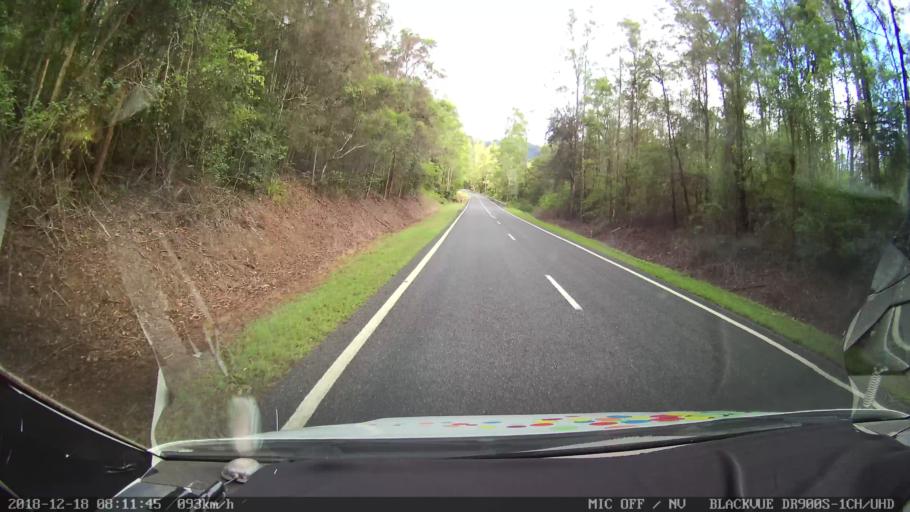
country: AU
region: New South Wales
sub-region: Kyogle
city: Kyogle
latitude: -28.3469
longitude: 152.6701
